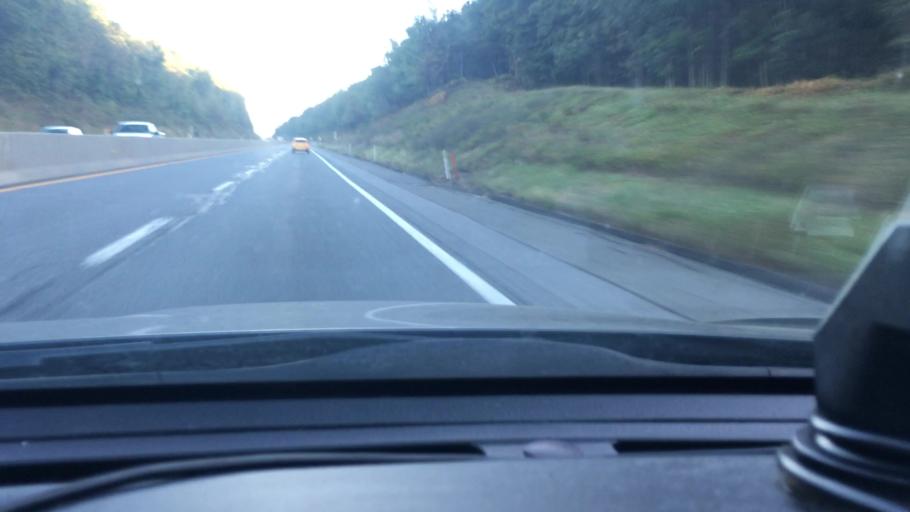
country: US
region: Pennsylvania
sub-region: Carbon County
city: Weissport East
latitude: 40.9224
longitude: -75.6469
